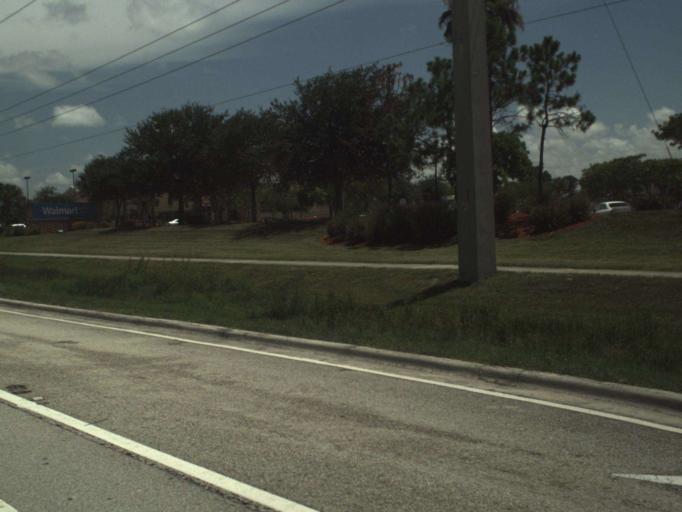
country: US
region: Florida
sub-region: Martin County
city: North River Shores
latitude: 27.2663
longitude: -80.2858
